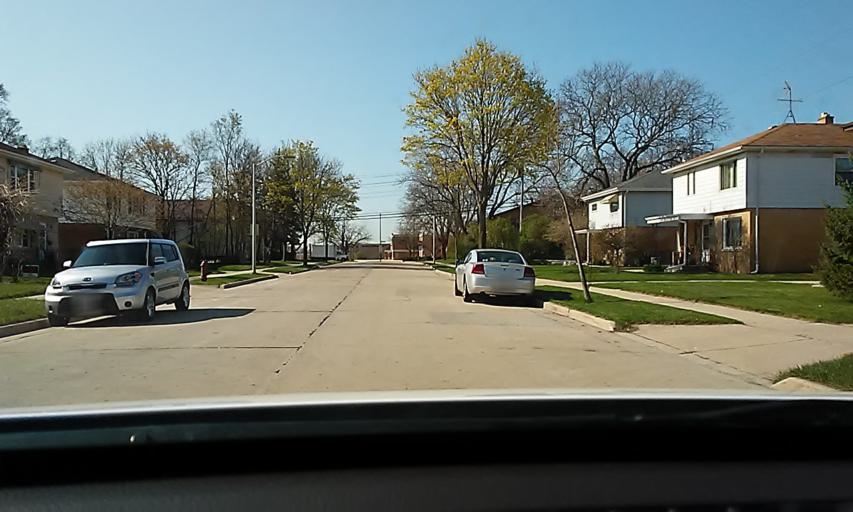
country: US
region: Wisconsin
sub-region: Waukesha County
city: Elm Grove
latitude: 43.0177
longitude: -88.0509
